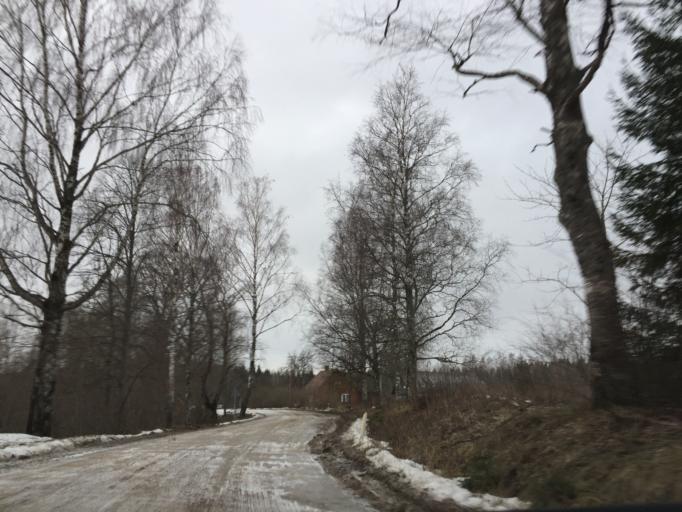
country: LV
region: Salacgrivas
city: Salacgriva
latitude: 57.6531
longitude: 24.4568
